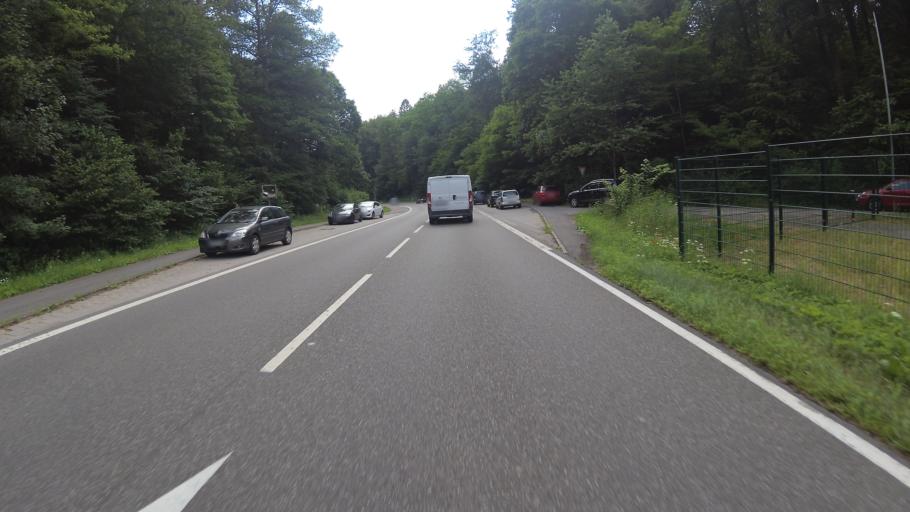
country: DE
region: Saarland
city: Homburg
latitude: 49.3055
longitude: 7.3525
